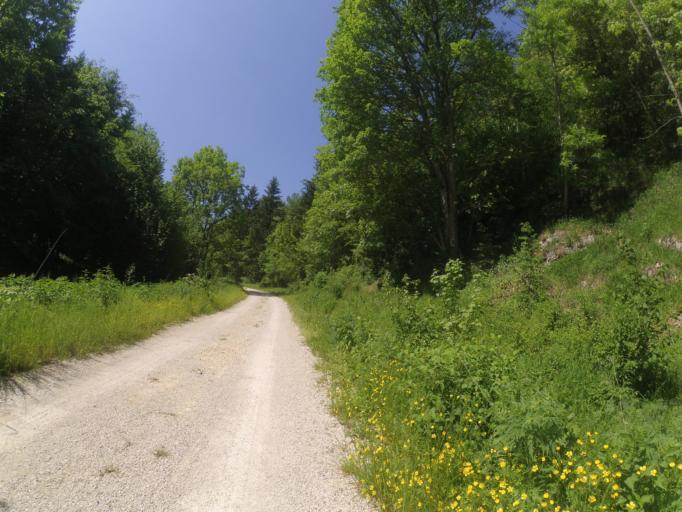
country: DE
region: Baden-Wuerttemberg
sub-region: Tuebingen Region
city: Berghulen
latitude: 48.4833
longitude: 9.8049
